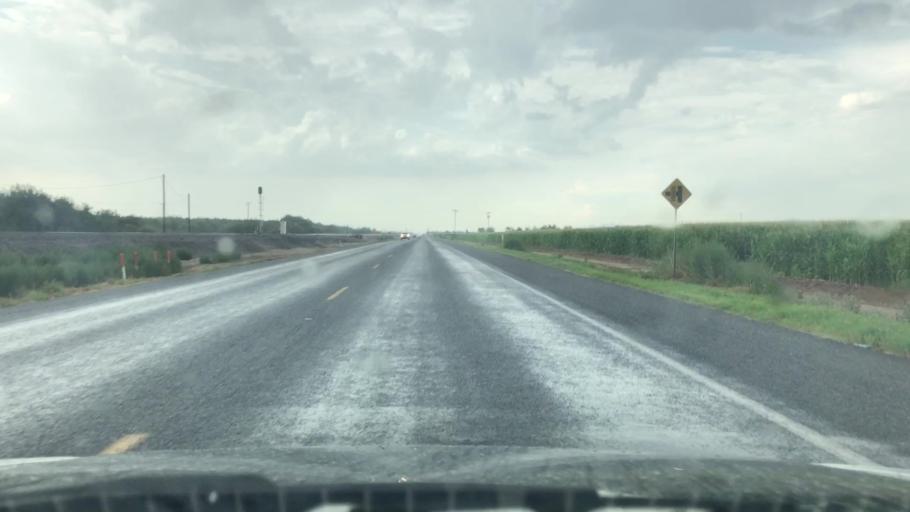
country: US
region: New Mexico
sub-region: Dona Ana County
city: Mesquite
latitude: 32.1434
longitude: -106.6832
